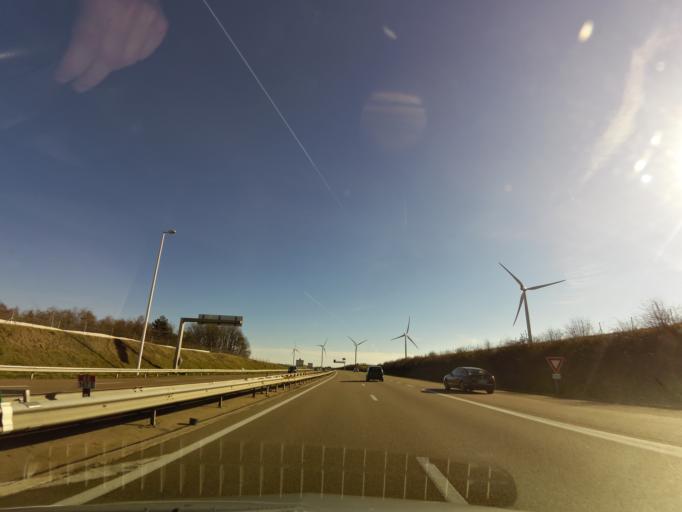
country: FR
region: Bourgogne
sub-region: Departement de l'Yonne
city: Venoy
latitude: 47.7856
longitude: 3.6750
